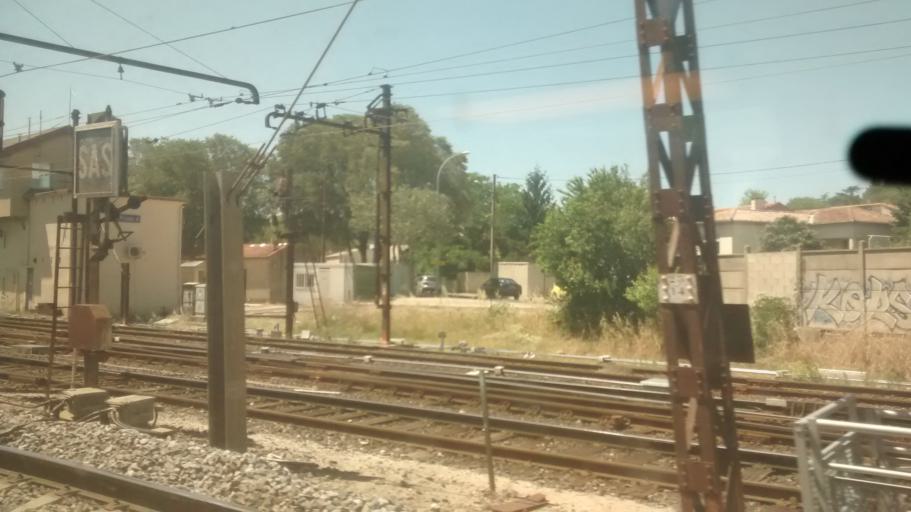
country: FR
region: Languedoc-Roussillon
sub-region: Departement du Gard
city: Nimes
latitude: 43.8455
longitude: 4.3799
